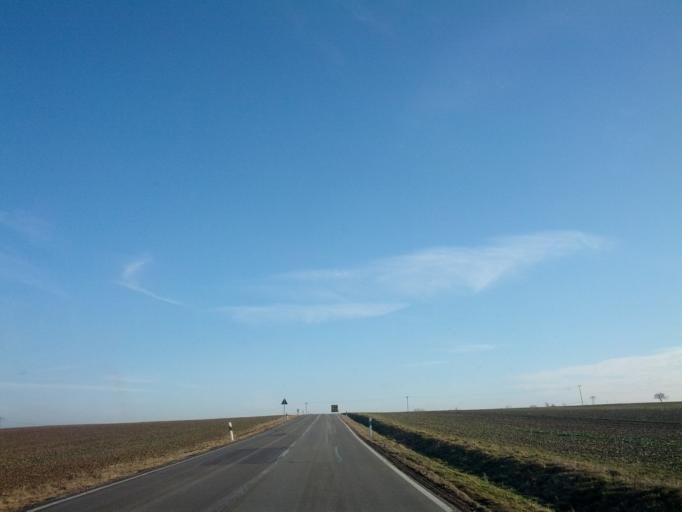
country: DE
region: Thuringia
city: Schonstedt
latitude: 51.0934
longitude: 10.5593
